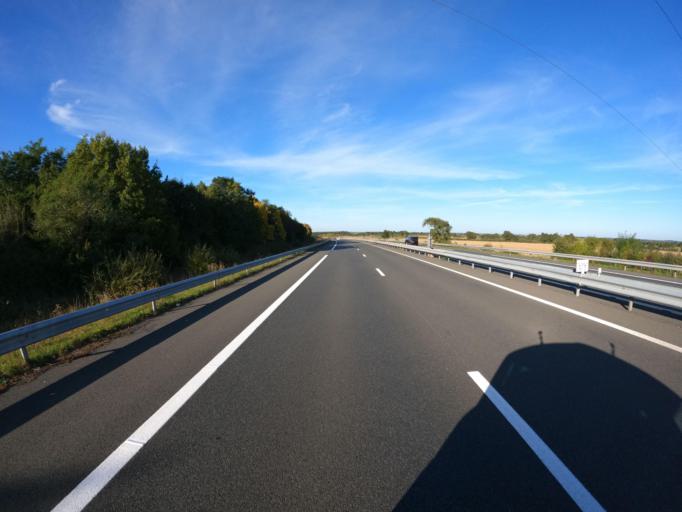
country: FR
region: Pays de la Loire
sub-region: Departement de Maine-et-Loire
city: Saint-Lambert-du-Lattay
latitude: 47.2589
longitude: -0.6173
